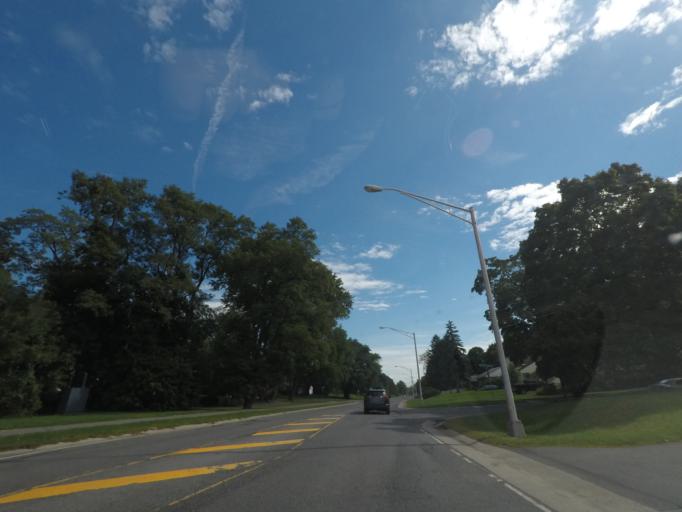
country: US
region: New York
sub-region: Albany County
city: West Albany
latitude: 42.6499
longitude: -73.7979
